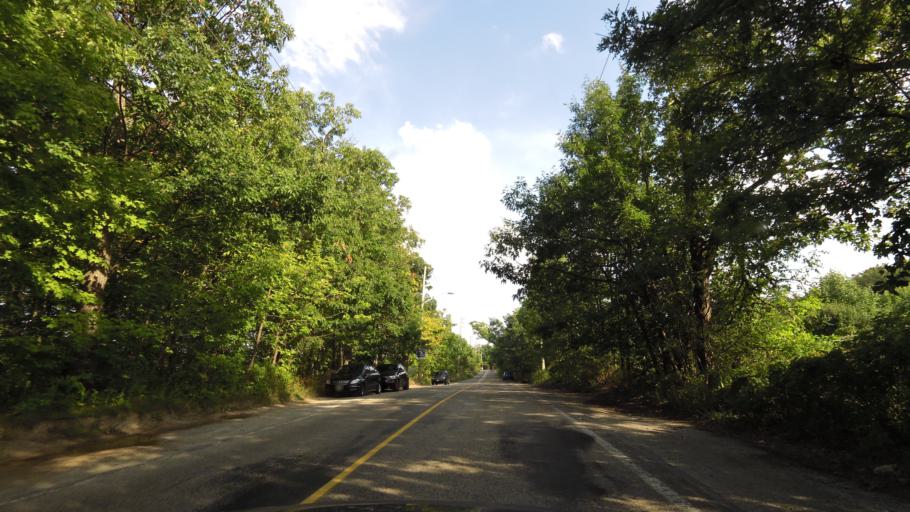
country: CA
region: Ontario
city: Burlington
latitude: 43.3490
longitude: -79.8629
